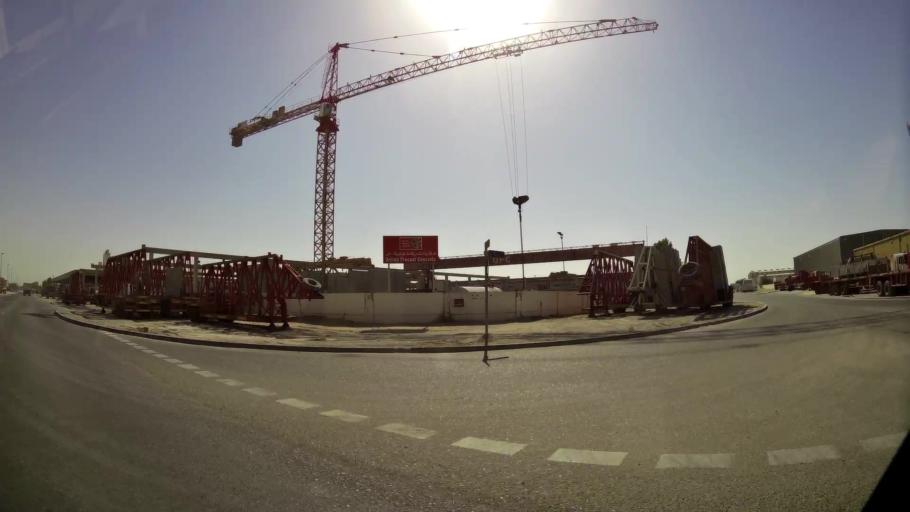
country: AE
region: Dubai
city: Dubai
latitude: 25.1221
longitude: 55.2203
